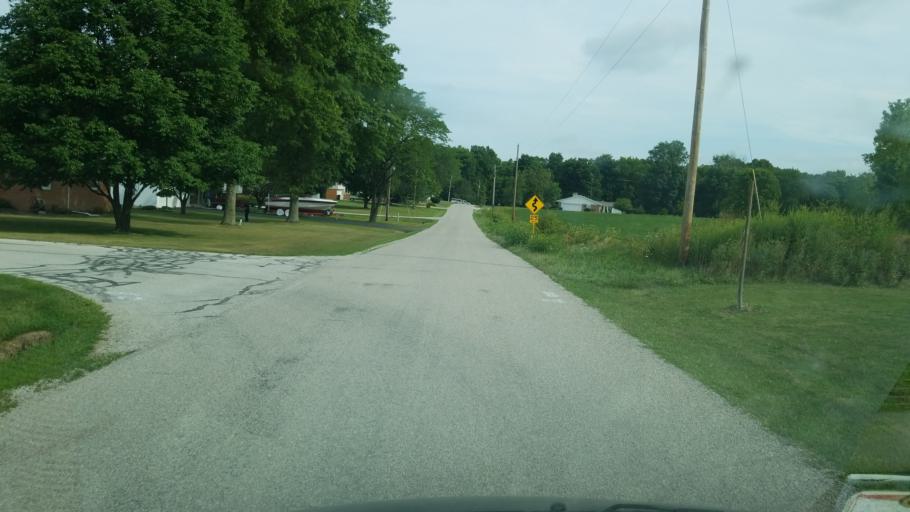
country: US
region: Ohio
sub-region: Seneca County
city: Tiffin
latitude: 41.1277
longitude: -83.0933
